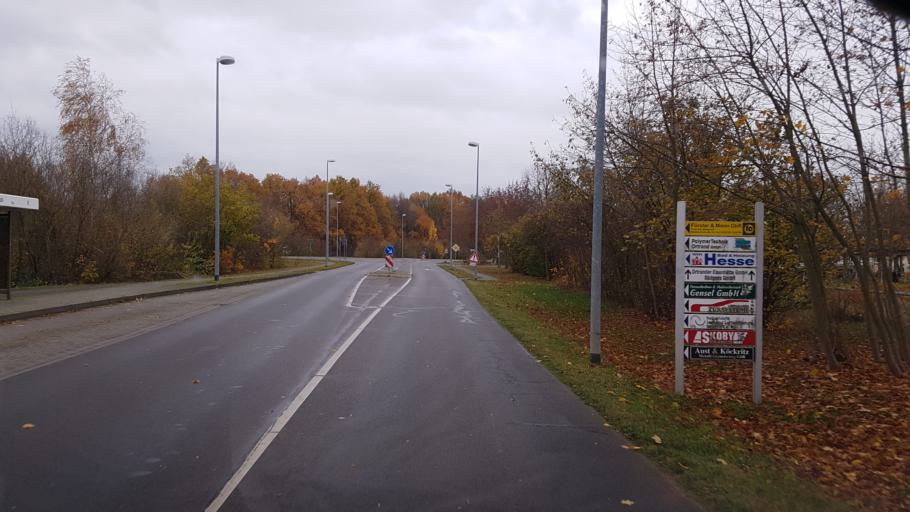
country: DE
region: Brandenburg
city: Ortrand
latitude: 51.3795
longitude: 13.7685
